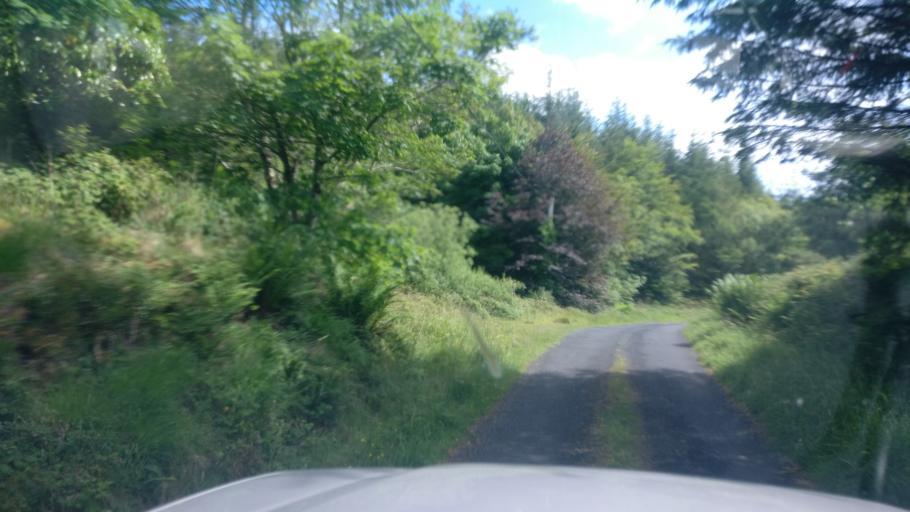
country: IE
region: Connaught
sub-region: County Galway
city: Gort
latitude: 53.0757
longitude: -8.7089
